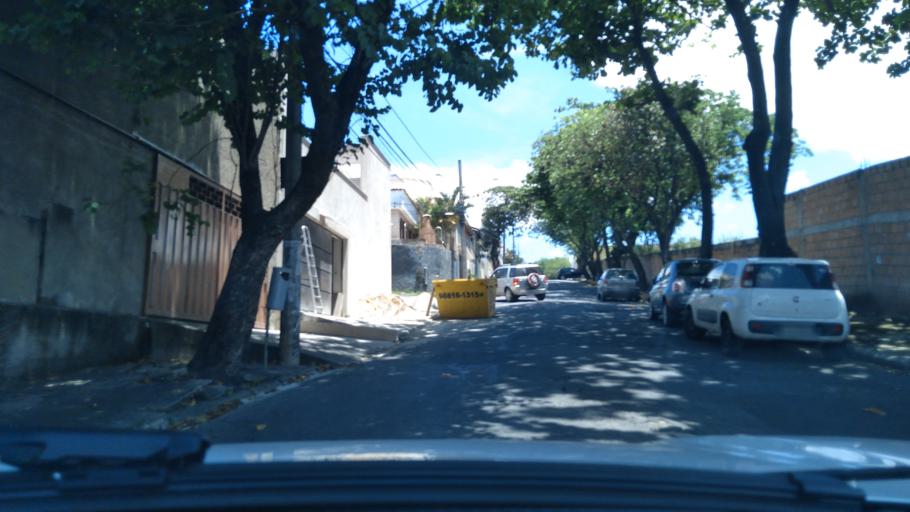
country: BR
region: Minas Gerais
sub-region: Contagem
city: Contagem
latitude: -19.9251
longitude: -43.9970
